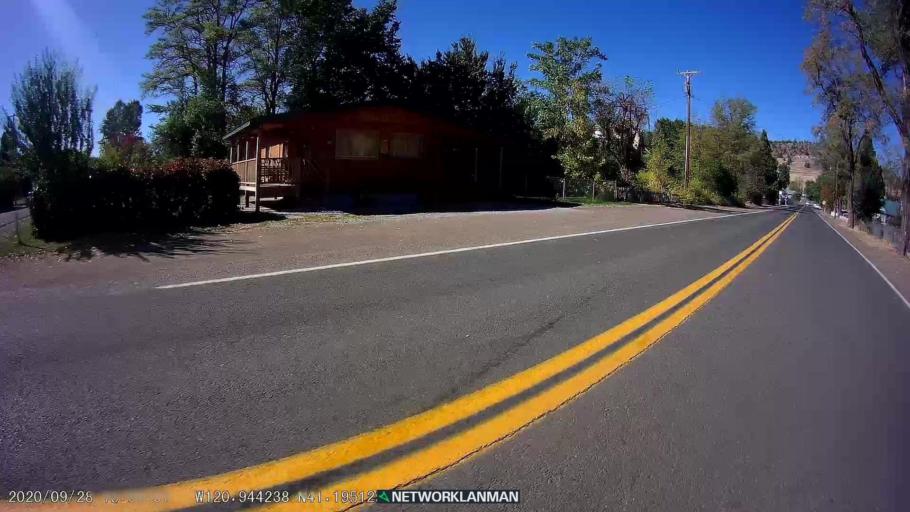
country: US
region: California
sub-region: Modoc County
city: Alturas
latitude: 41.1954
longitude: -120.9442
